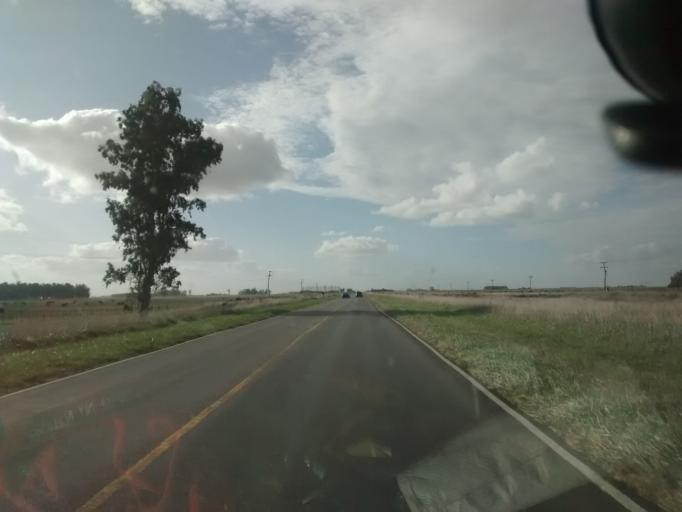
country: AR
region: Buenos Aires
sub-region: Partido de Ayacucho
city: Ayacucho
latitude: -36.9124
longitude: -58.5251
